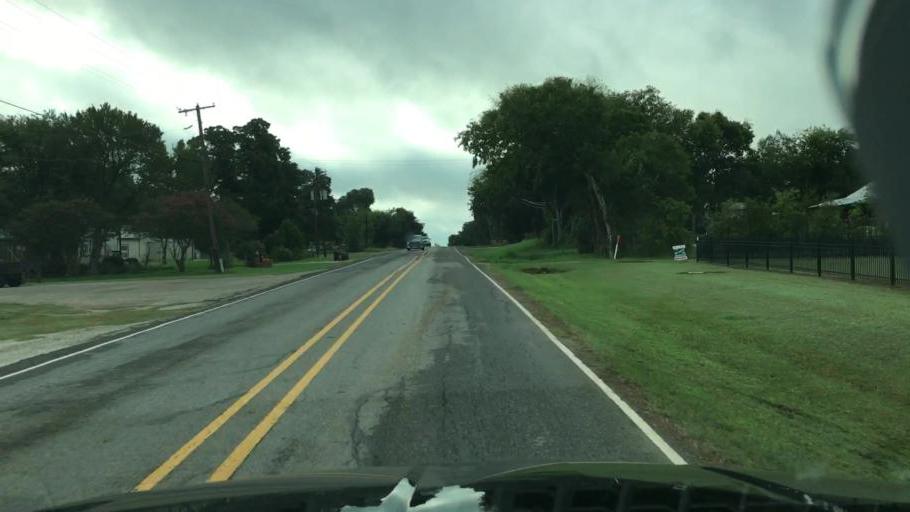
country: US
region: Texas
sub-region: Lee County
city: Lexington
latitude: 30.3638
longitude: -96.8333
